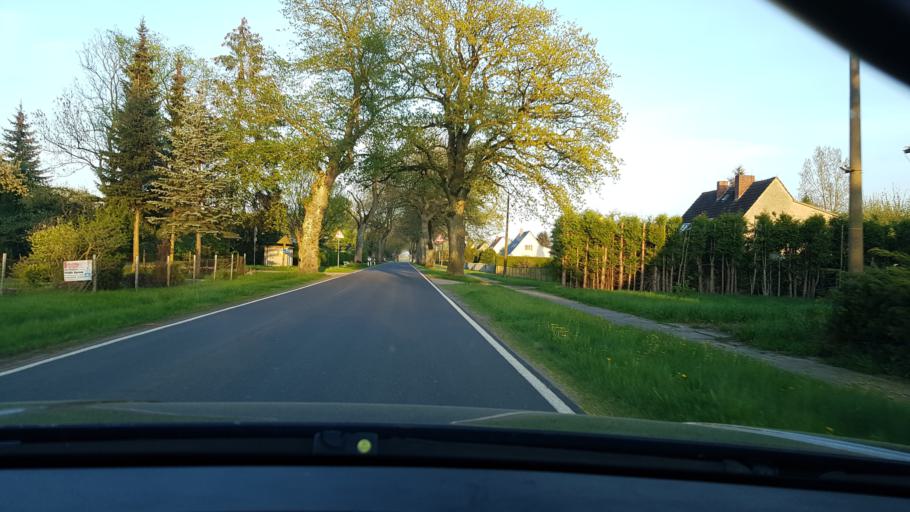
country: DE
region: Mecklenburg-Vorpommern
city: Alt-Sanitz
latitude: 53.8948
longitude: 13.5898
